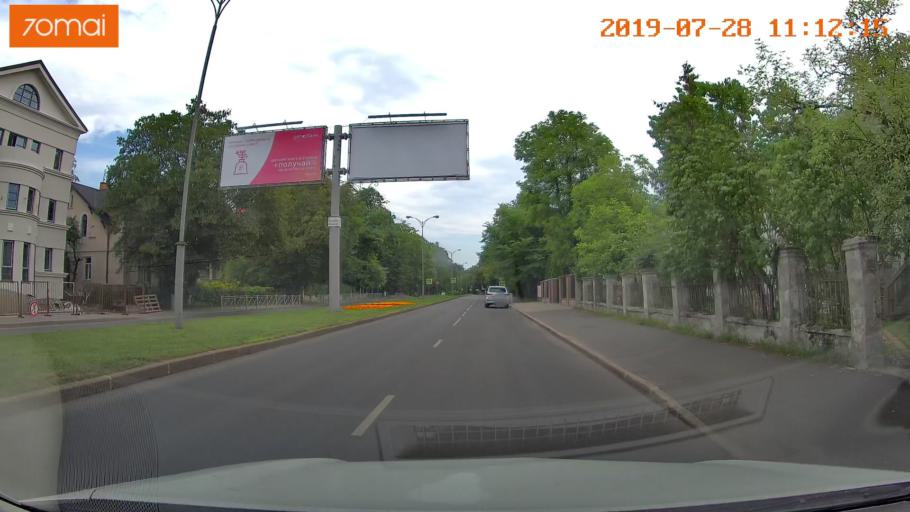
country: RU
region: Kaliningrad
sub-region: Gorod Kaliningrad
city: Kaliningrad
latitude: 54.7181
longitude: 20.4662
